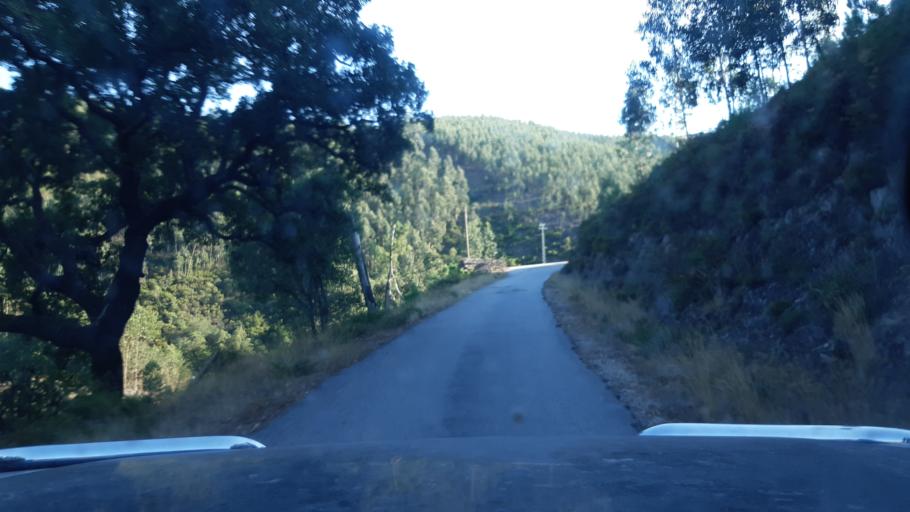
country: PT
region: Viseu
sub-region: Mortagua
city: Mortagua
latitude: 40.5323
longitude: -8.2525
